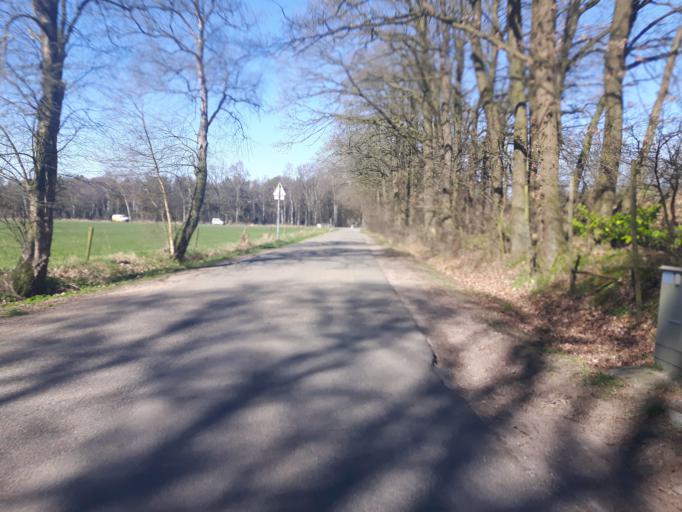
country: NL
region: Overijssel
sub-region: Gemeente Enschede
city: Enschede
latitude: 52.1711
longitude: 6.8243
